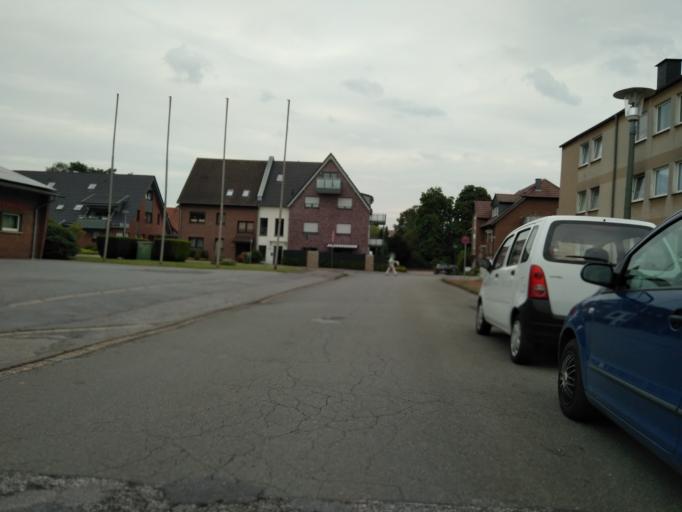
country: DE
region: North Rhine-Westphalia
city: Dorsten
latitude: 51.6051
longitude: 6.9191
